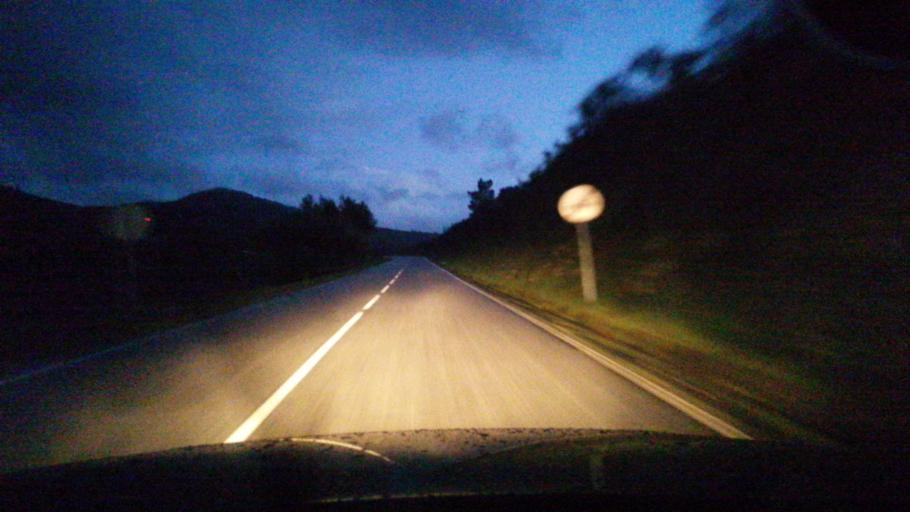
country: PT
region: Viseu
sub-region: Tabuaco
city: Tabuaco
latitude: 41.1449
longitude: -7.5383
